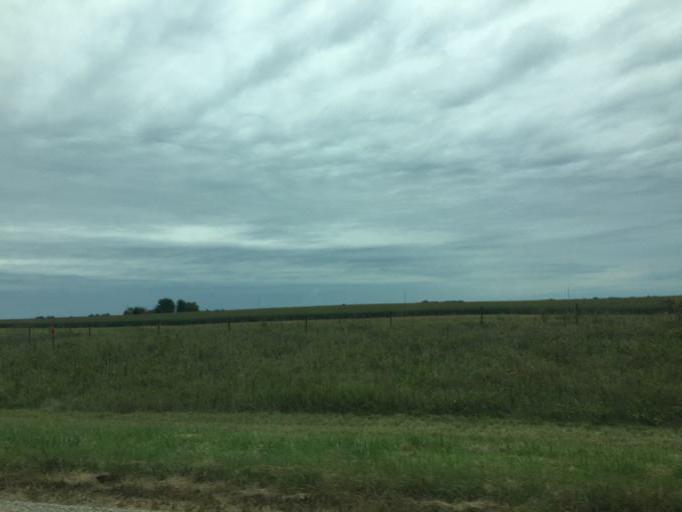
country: US
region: Minnesota
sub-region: Winona County
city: Lewiston
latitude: 43.9398
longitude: -91.7638
